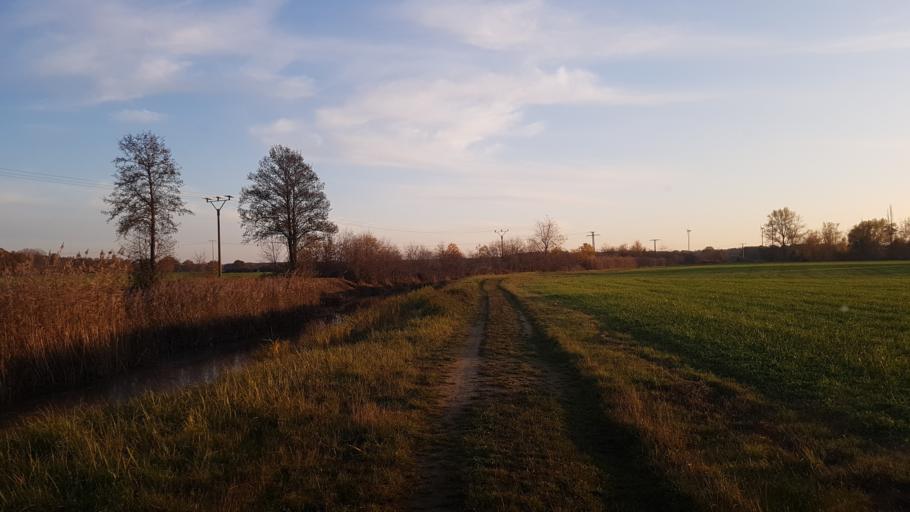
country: DE
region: Brandenburg
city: Schilda
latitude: 51.6034
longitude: 13.3154
